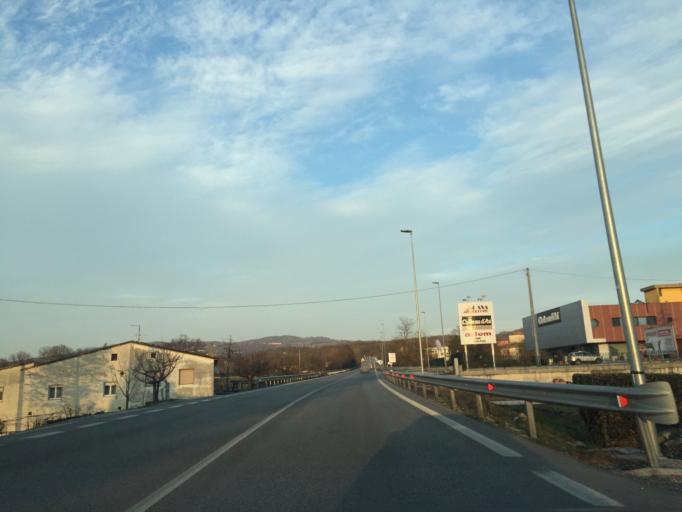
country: IT
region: Molise
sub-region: Provincia di Campobasso
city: Vinchiaturo
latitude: 41.4791
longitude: 14.5786
